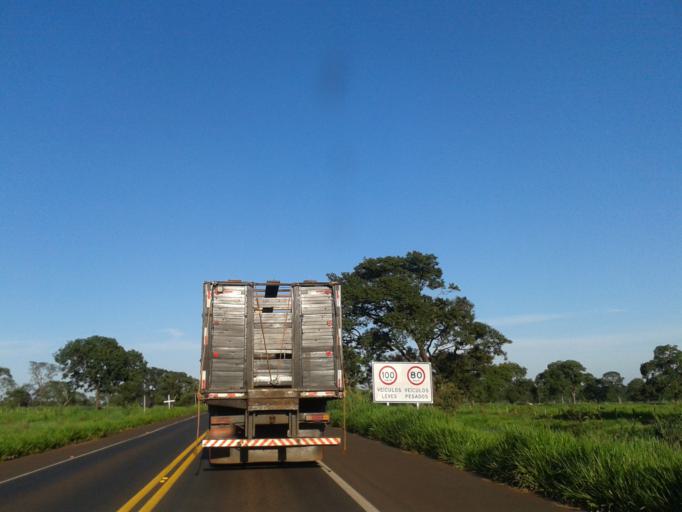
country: BR
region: Minas Gerais
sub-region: Santa Vitoria
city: Santa Vitoria
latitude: -18.9360
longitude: -49.8253
